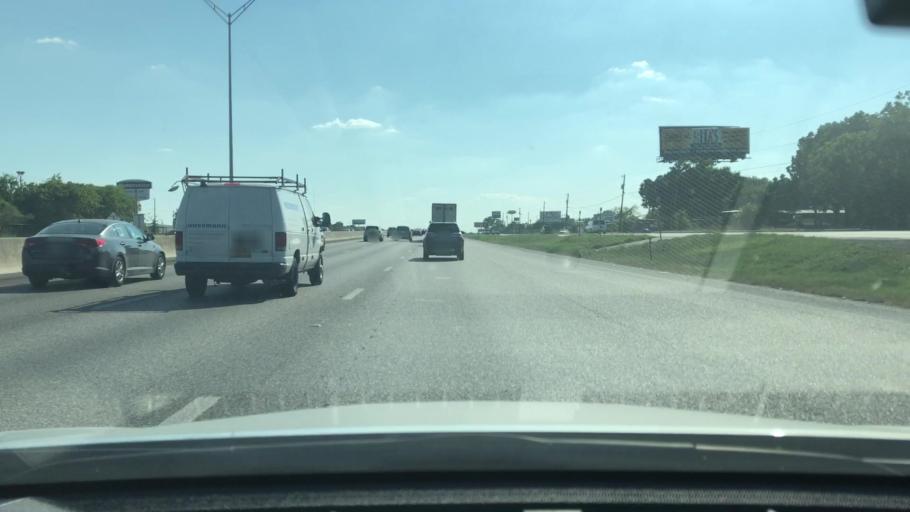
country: US
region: Texas
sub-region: Comal County
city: New Braunfels
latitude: 29.6606
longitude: -98.1734
